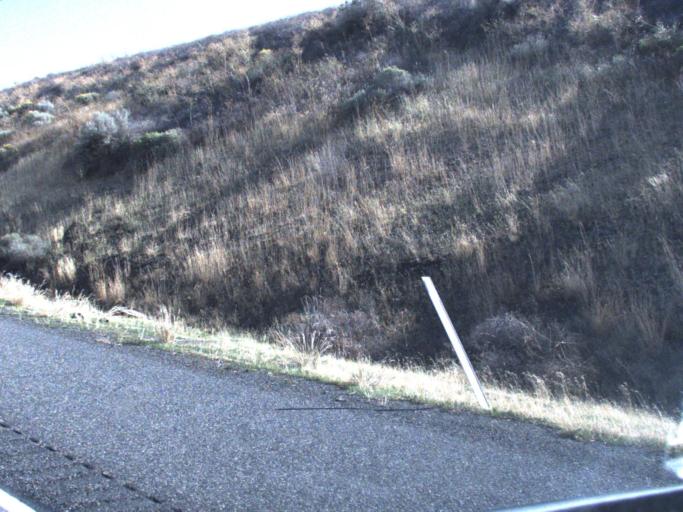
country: US
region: Washington
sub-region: Franklin County
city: West Pasco
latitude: 46.1825
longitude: -119.2447
